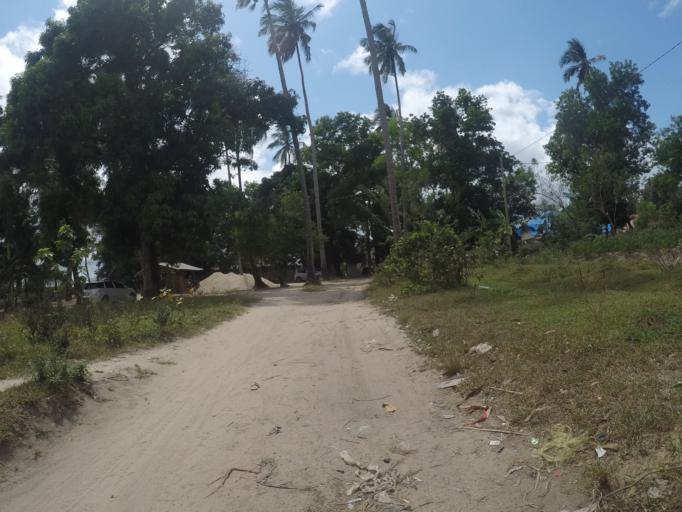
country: TZ
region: Zanzibar Urban/West
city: Zanzibar
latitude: -6.2051
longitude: 39.2428
